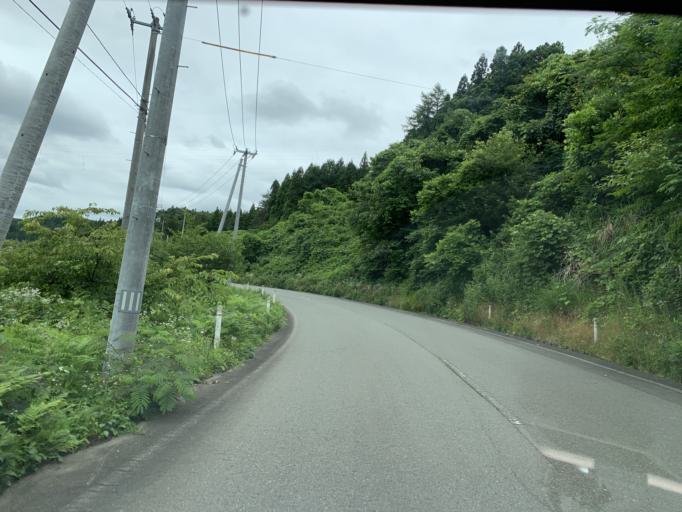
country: JP
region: Iwate
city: Ichinoseki
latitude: 38.9013
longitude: 140.9928
